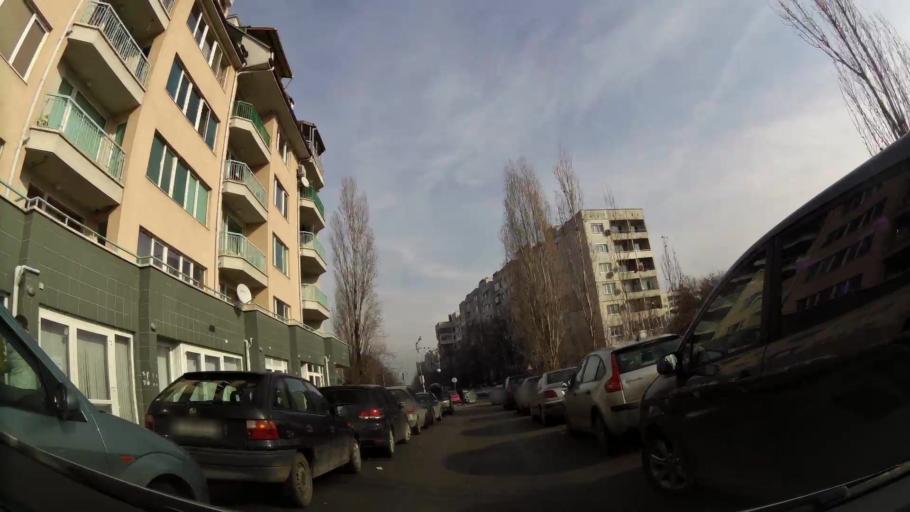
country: BG
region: Sofiya
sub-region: Obshtina Bozhurishte
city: Bozhurishte
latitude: 42.7188
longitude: 23.2588
